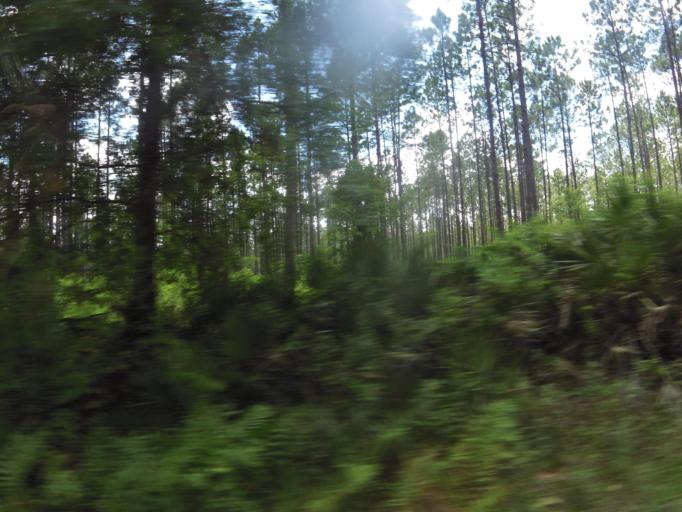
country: US
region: Florida
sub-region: Clay County
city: Asbury Lake
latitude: 29.8749
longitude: -81.8529
